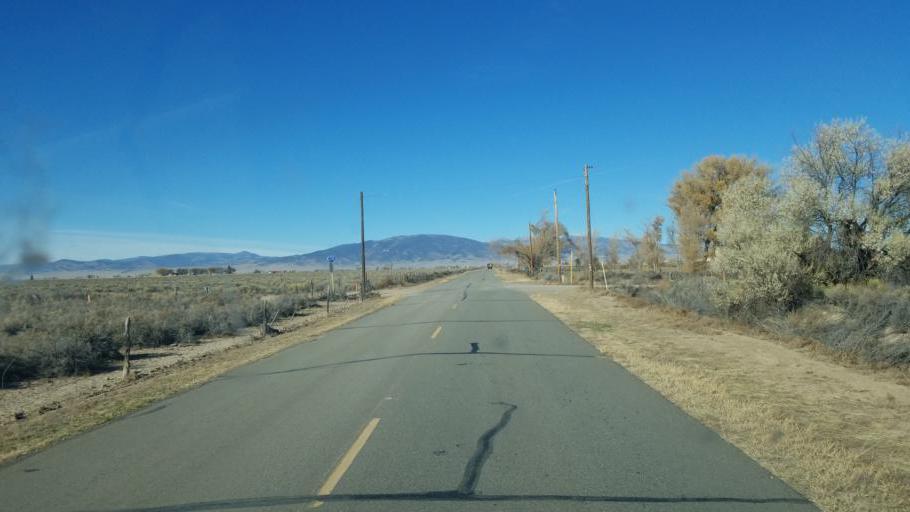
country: US
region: Colorado
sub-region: Alamosa County
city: Alamosa
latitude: 37.4586
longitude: -106.0202
